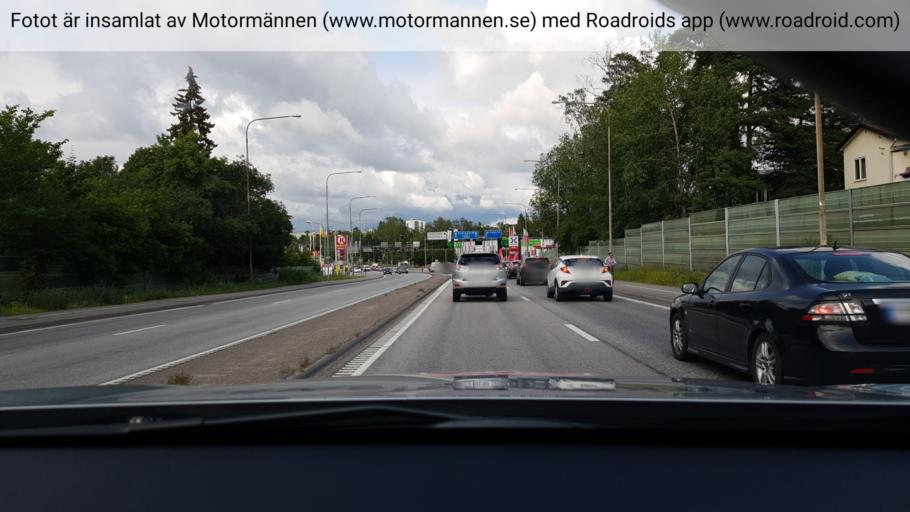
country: SE
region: Stockholm
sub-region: Huddinge Kommun
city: Huddinge
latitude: 59.2479
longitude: 18.0084
